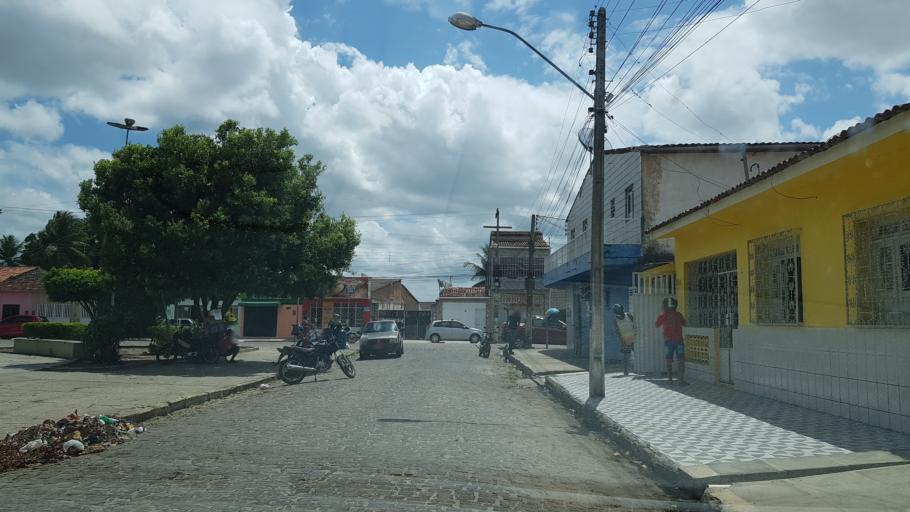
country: BR
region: Alagoas
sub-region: Penedo
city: Penedo
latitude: -10.2794
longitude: -36.5634
